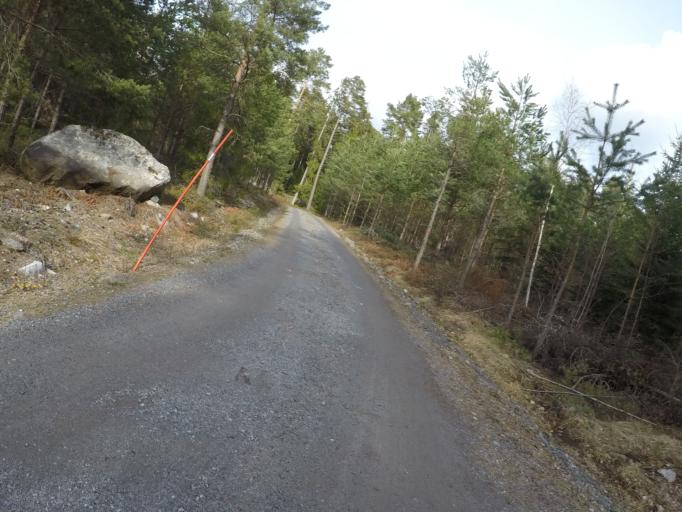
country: SE
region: Soedermanland
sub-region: Eskilstuna Kommun
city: Torshalla
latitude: 59.4496
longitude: 16.5531
